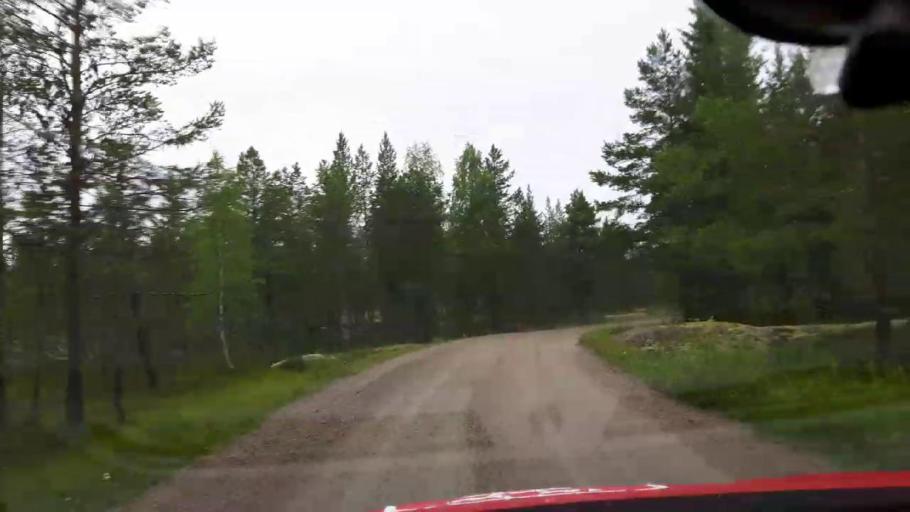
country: SE
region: Jaemtland
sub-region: OEstersunds Kommun
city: Brunflo
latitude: 62.8121
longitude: 14.8834
